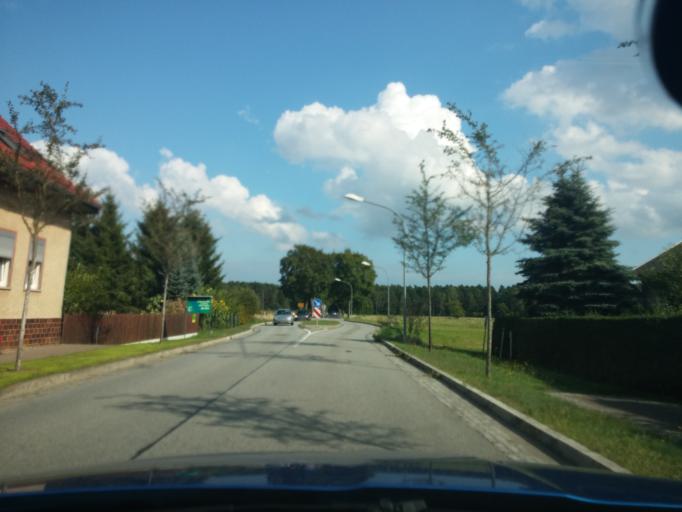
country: DE
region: Brandenburg
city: Halbe
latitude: 52.1082
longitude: 13.7707
